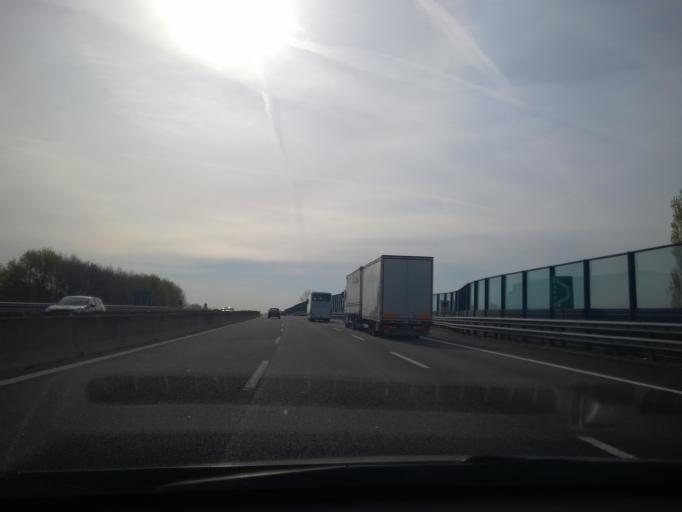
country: IT
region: Emilia-Romagna
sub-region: Forli-Cesena
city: Santa Maria Nuova
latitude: 44.2077
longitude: 12.1930
